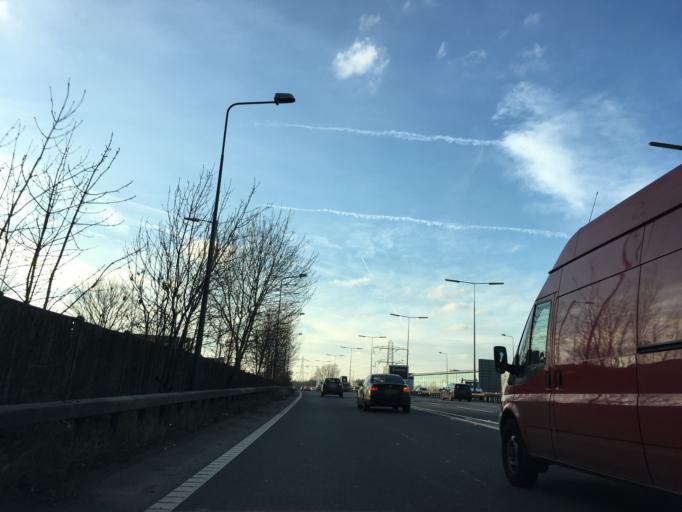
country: GB
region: England
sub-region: Borough of Stockport
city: Cheadle Heath
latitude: 53.4086
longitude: -2.1780
